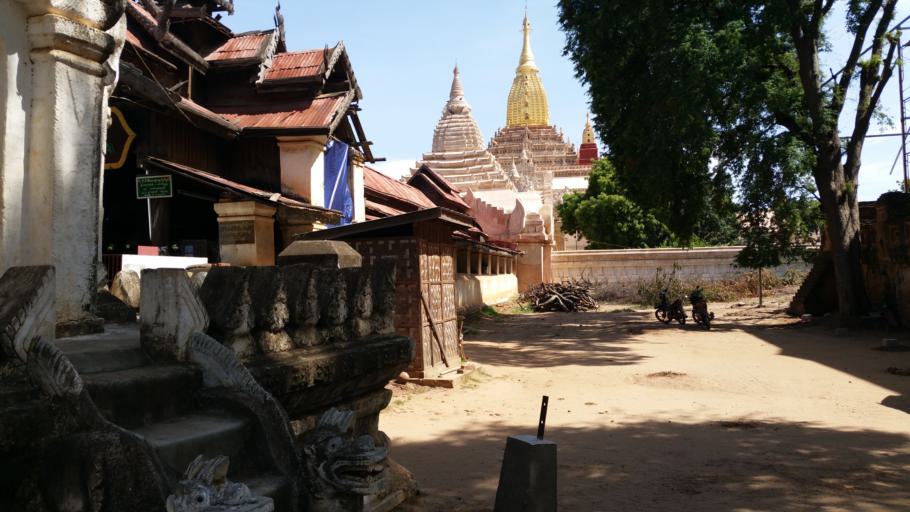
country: MM
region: Magway
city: Pakokku
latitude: 21.1720
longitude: 94.8674
